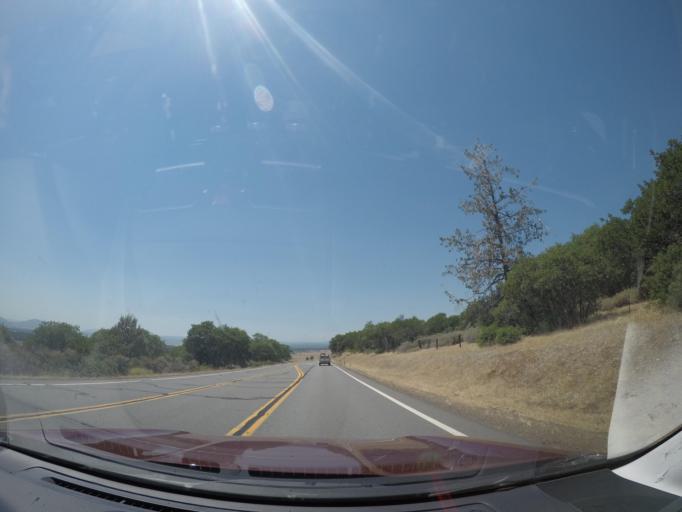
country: US
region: California
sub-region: Shasta County
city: Burney
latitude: 41.0932
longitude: -121.2752
